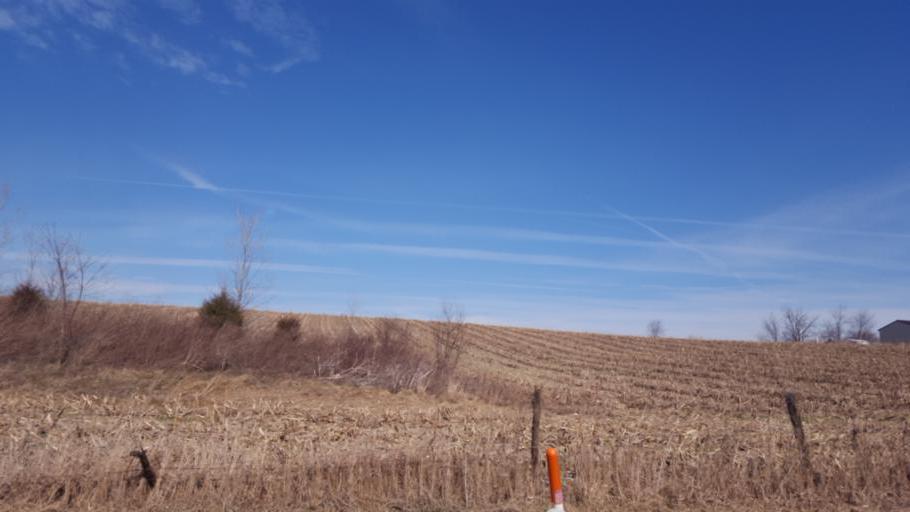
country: US
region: Ohio
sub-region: Knox County
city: Gambier
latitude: 40.5083
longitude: -82.4009
